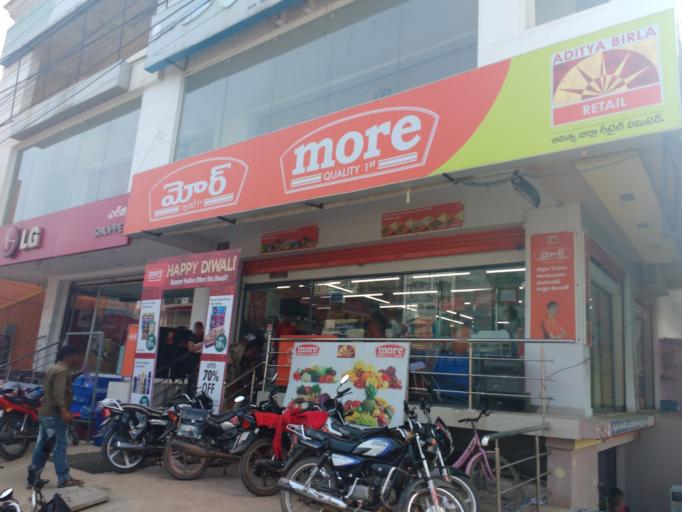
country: IN
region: Andhra Pradesh
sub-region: Kurnool
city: Nandyal
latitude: 15.4863
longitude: 78.4826
